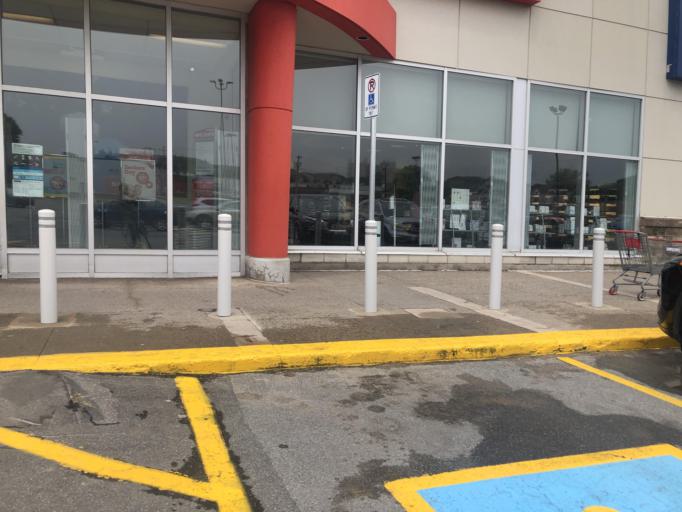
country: CA
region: New Brunswick
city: Saint John
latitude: 45.2768
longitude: -66.0787
